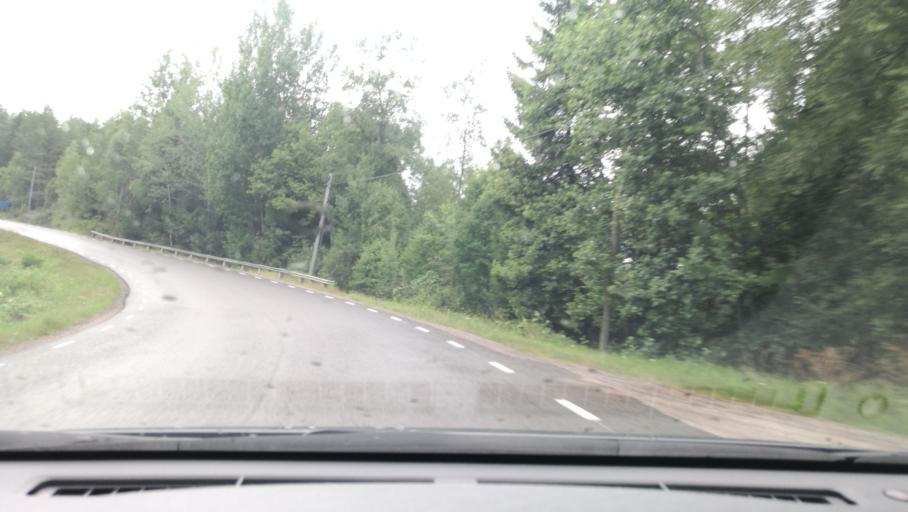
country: SE
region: OEstergoetland
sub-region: Norrkopings Kommun
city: Jursla
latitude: 58.8108
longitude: 16.0977
